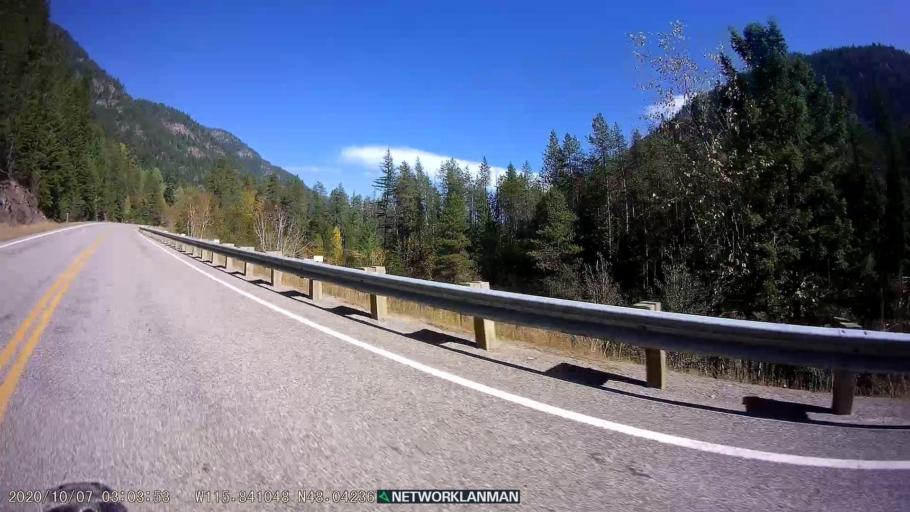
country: US
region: Montana
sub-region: Lincoln County
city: Libby
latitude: 48.0427
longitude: -115.8410
